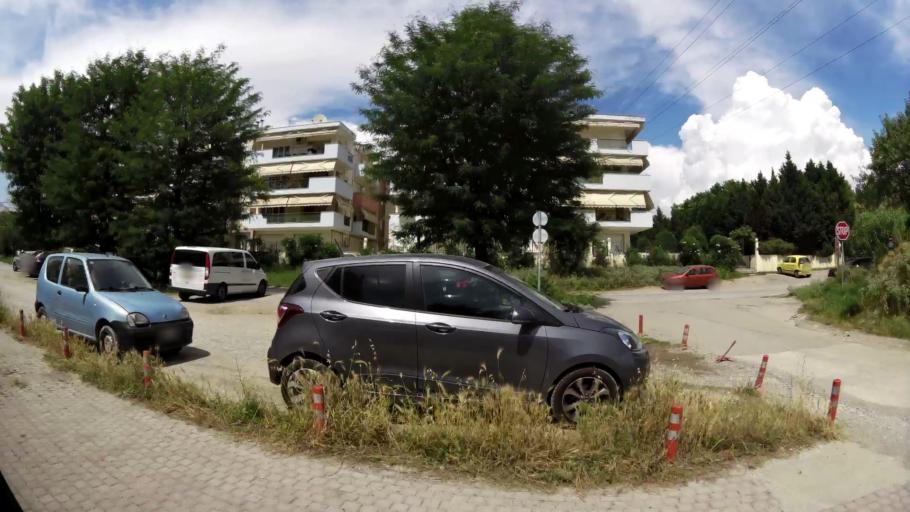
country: GR
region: Central Macedonia
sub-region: Nomos Thessalonikis
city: Pylaia
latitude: 40.5931
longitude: 22.9772
